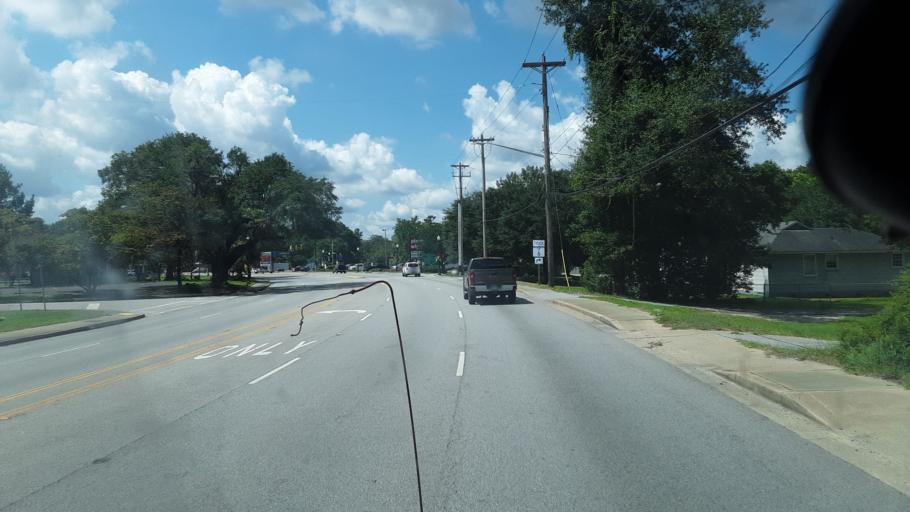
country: US
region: South Carolina
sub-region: Berkeley County
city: Moncks Corner
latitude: 33.1973
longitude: -80.0114
